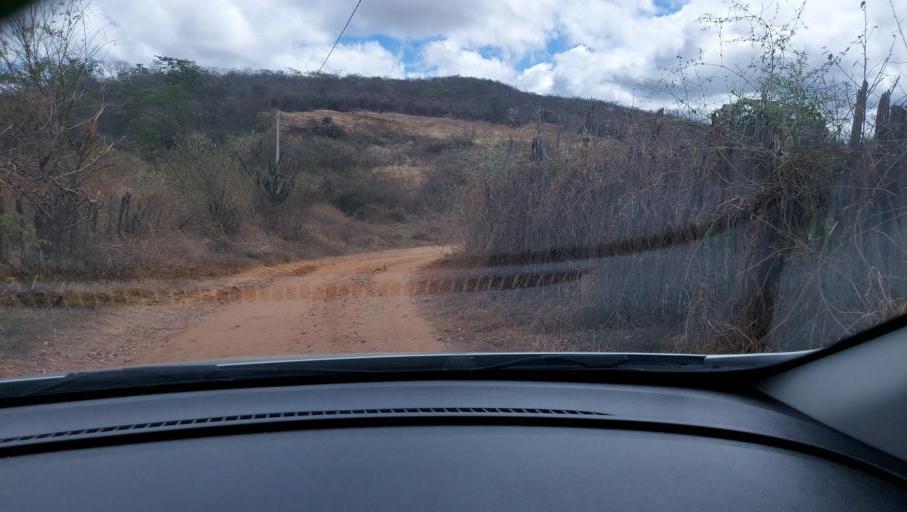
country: BR
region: Bahia
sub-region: Oliveira Dos Brejinhos
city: Beira Rio
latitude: -12.0742
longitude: -42.5416
